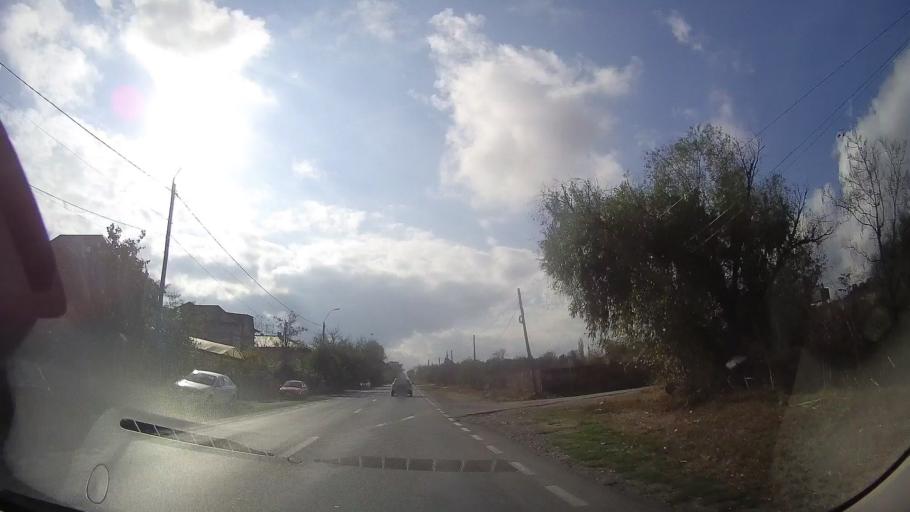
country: RO
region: Constanta
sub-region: Comuna Agigea
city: Agigea
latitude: 44.0882
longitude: 28.6098
